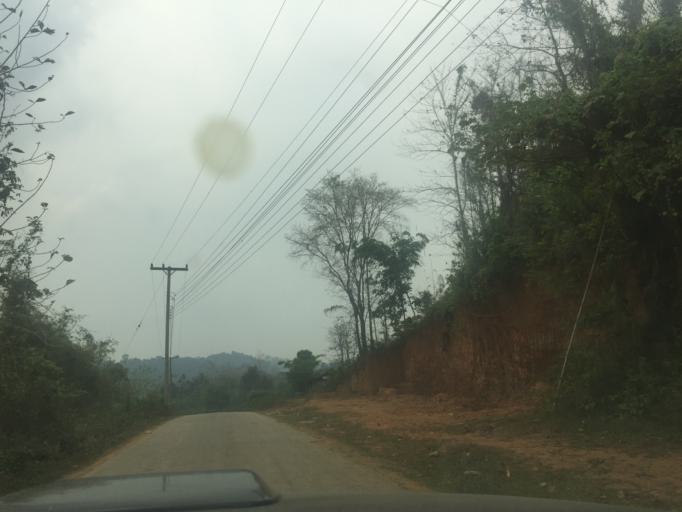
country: LA
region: Vientiane
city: Muang Sanakham
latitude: 18.3975
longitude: 101.5185
